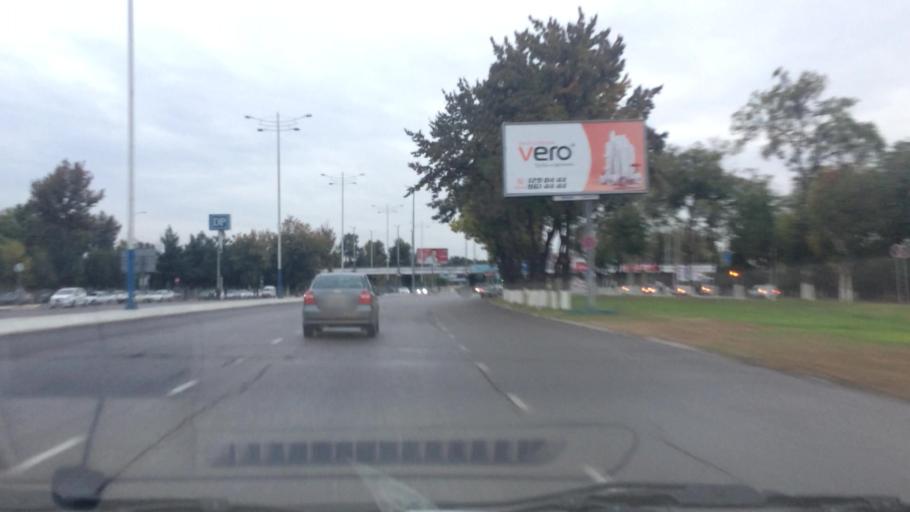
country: UZ
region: Toshkent Shahri
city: Tashkent
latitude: 41.2577
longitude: 69.1947
